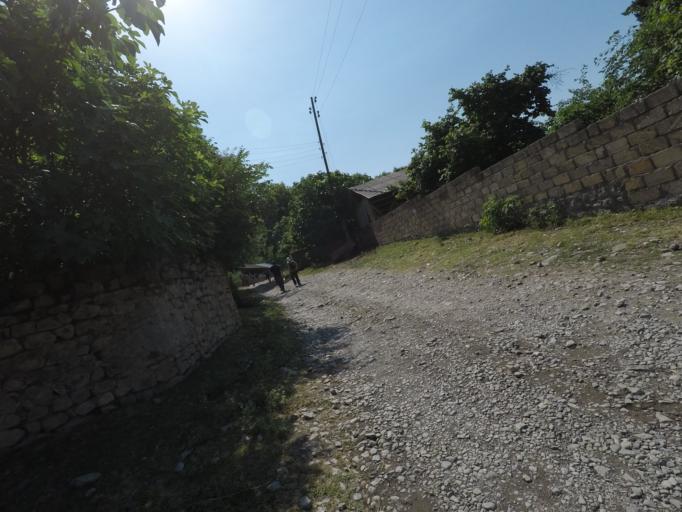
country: AZ
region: Qakh Rayon
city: Cinarli
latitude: 41.4836
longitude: 46.8472
